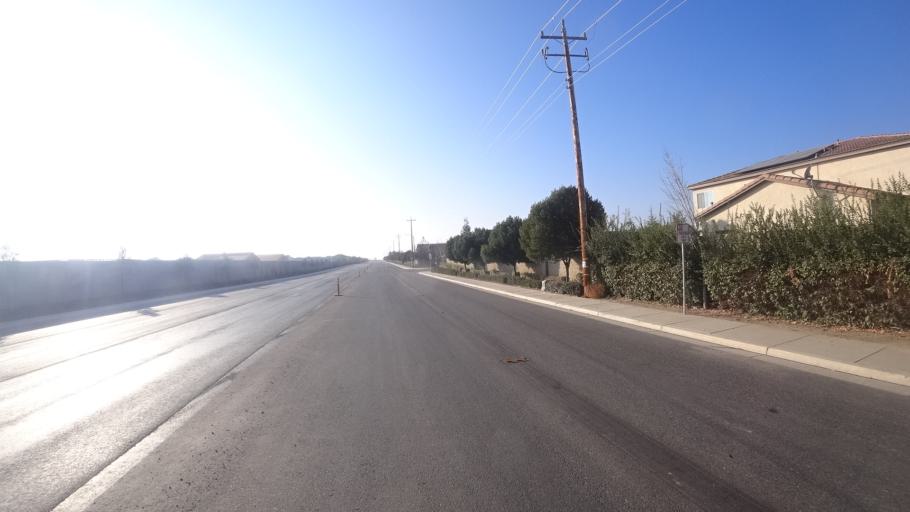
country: US
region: California
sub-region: Kern County
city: Greenacres
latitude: 35.2946
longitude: -119.1188
